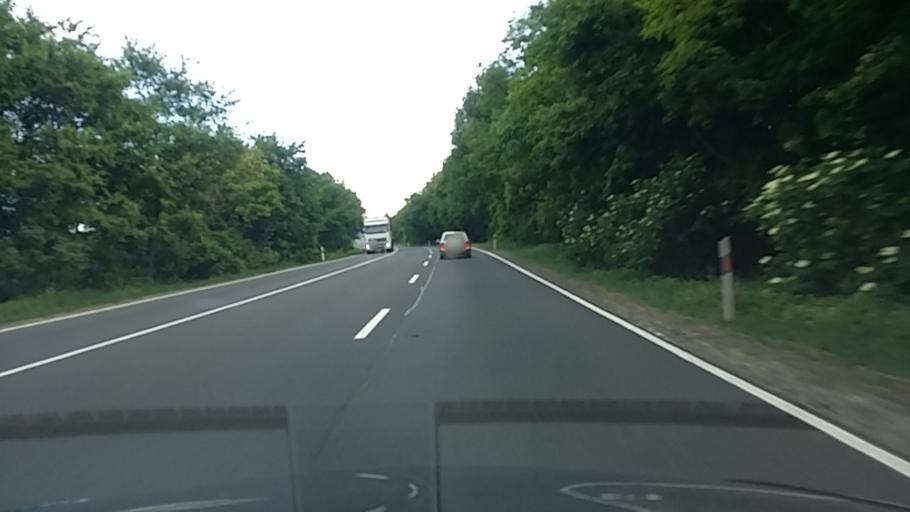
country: HU
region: Nograd
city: Retsag
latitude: 47.8887
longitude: 19.1016
